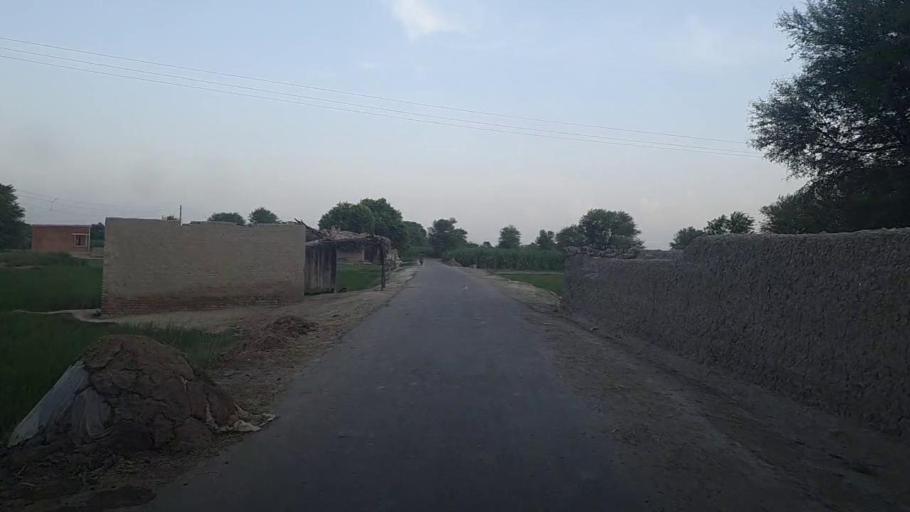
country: PK
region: Sindh
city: Ubauro
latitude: 28.3591
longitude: 69.7832
